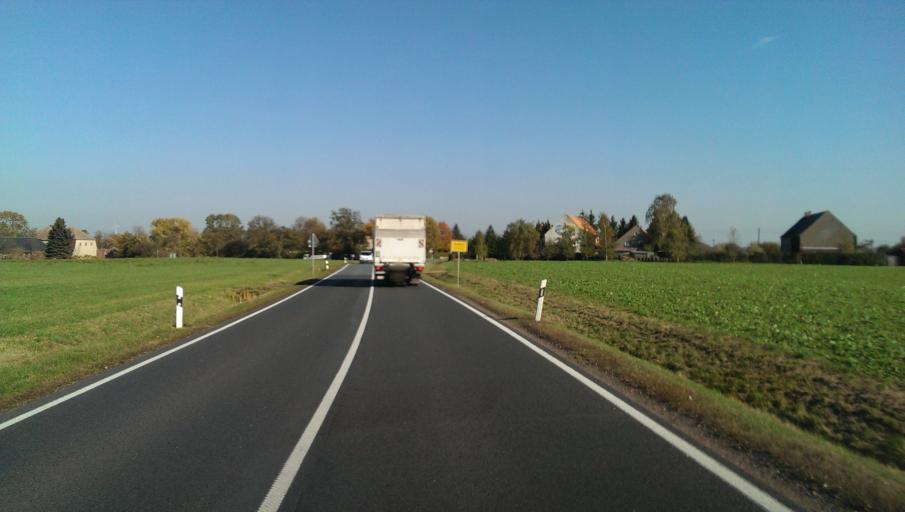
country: DE
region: Saxony
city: Ostrau
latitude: 51.2339
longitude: 13.1658
